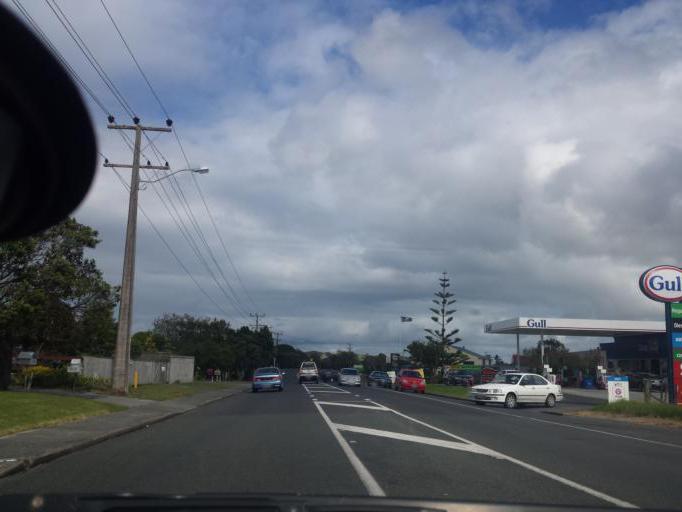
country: NZ
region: Auckland
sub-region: Auckland
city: Warkworth
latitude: -36.4170
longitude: 174.7237
